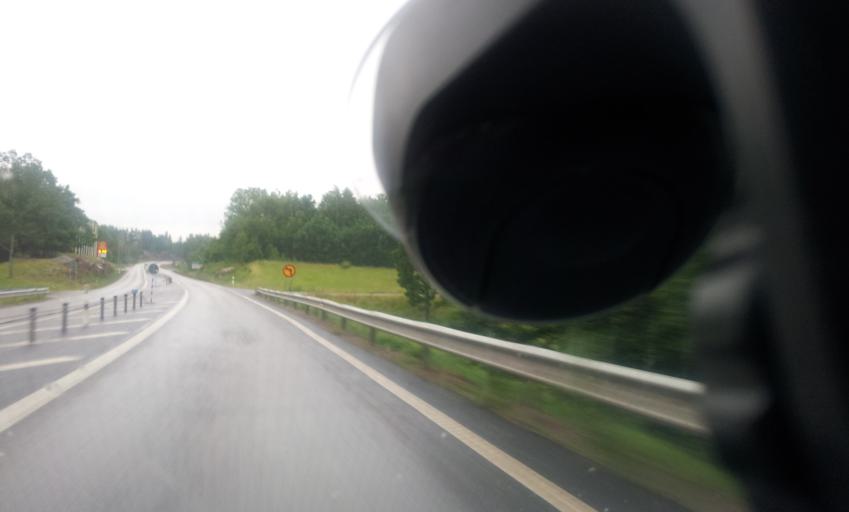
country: SE
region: Kalmar
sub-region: Vasterviks Kommun
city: Forserum
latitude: 57.9772
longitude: 16.4846
